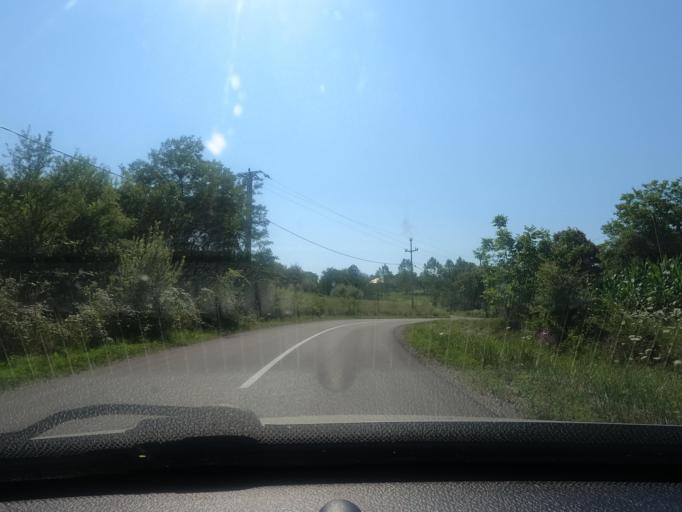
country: RS
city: Kozjak
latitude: 44.5446
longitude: 19.3034
